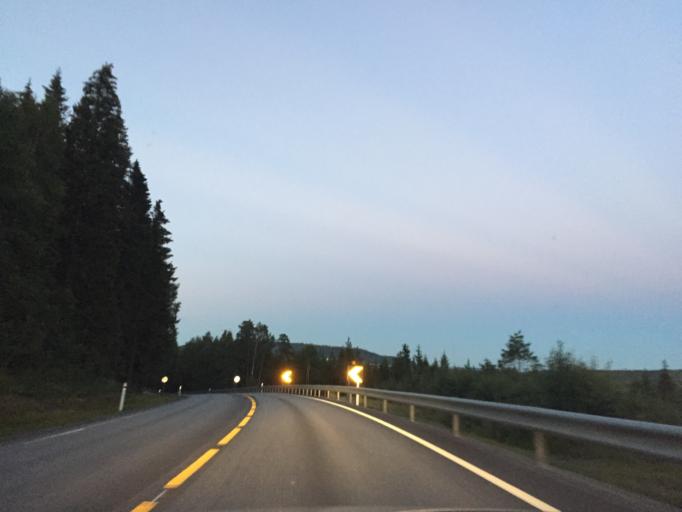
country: NO
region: Hedmark
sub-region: Kongsvinger
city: Spetalen
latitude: 60.2081
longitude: 11.8979
